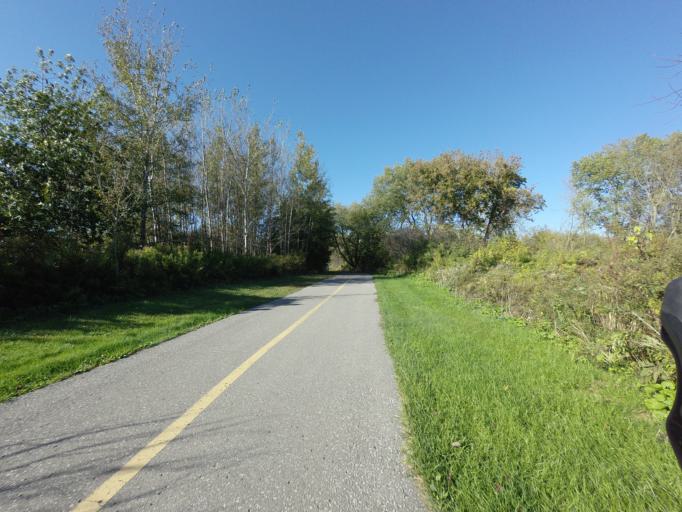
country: CA
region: Ontario
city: Oshawa
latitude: 43.8799
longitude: -78.8221
